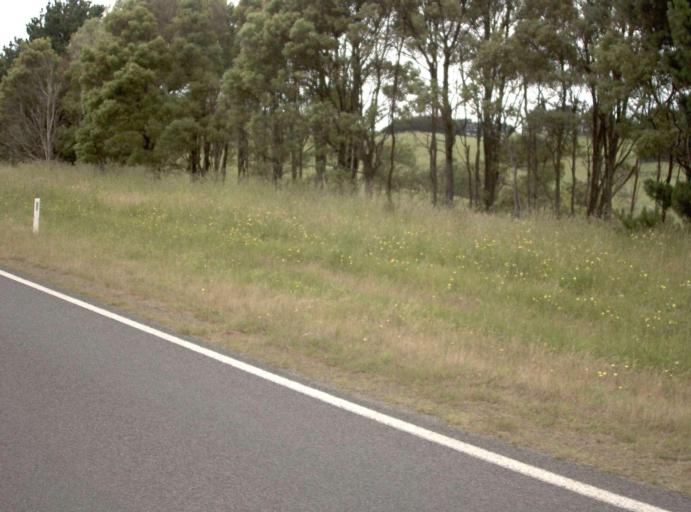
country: AU
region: Victoria
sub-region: Latrobe
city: Morwell
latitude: -38.6193
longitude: 146.1564
